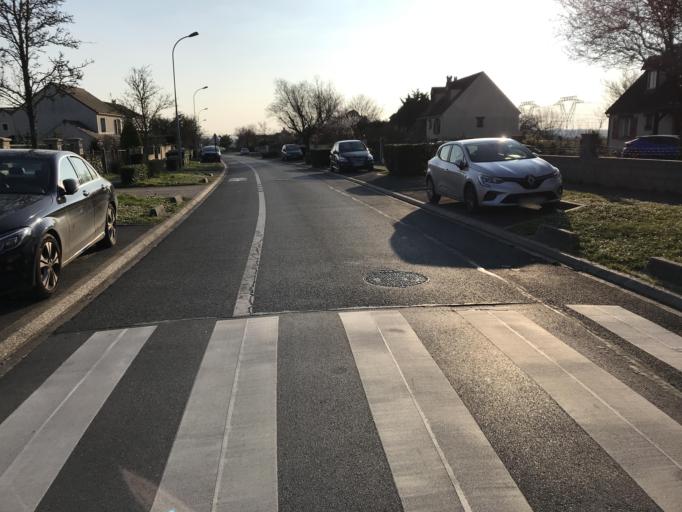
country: FR
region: Ile-de-France
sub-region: Departement de l'Essonne
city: Villejust
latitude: 48.6817
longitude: 2.2339
